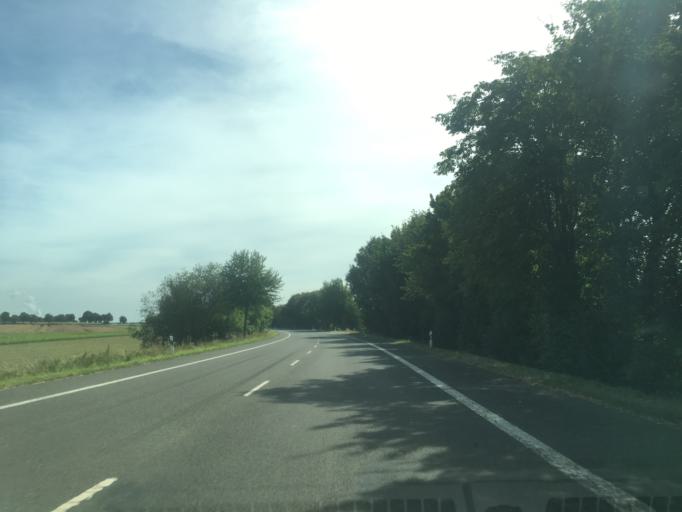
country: DE
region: North Rhine-Westphalia
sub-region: Regierungsbezirk Koln
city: Titz
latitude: 51.0410
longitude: 6.4000
